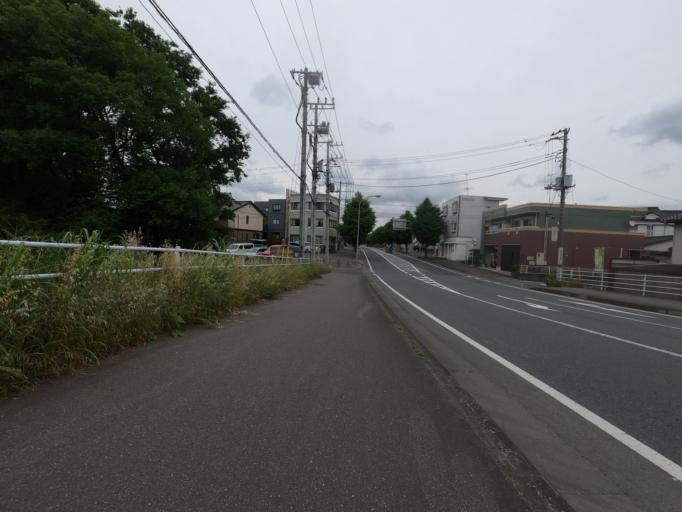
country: JP
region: Ibaraki
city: Moriya
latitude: 35.9469
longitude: 139.9799
